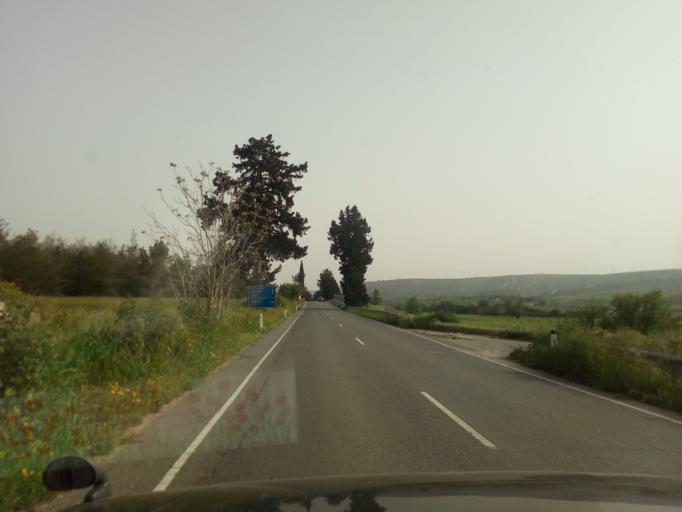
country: CY
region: Lefkosia
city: Lympia
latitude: 35.0045
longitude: 33.4985
